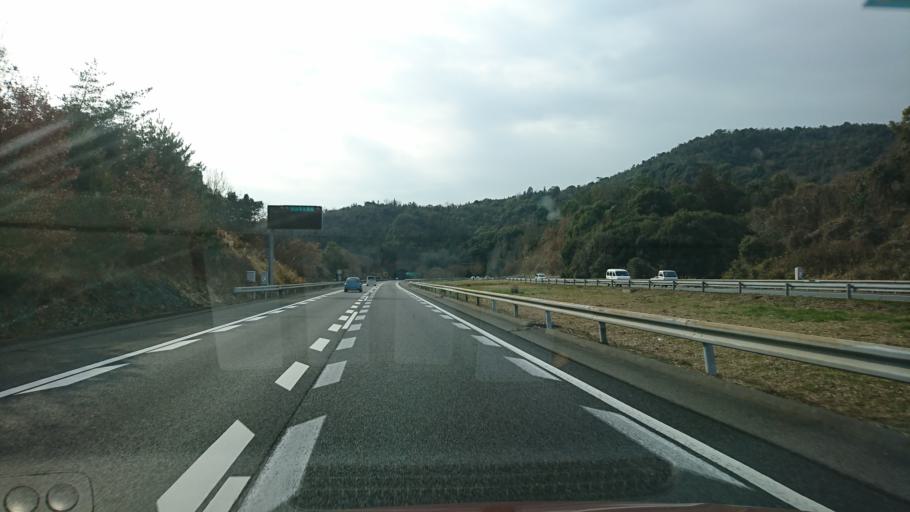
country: JP
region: Okayama
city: Soja
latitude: 34.6451
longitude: 133.8082
